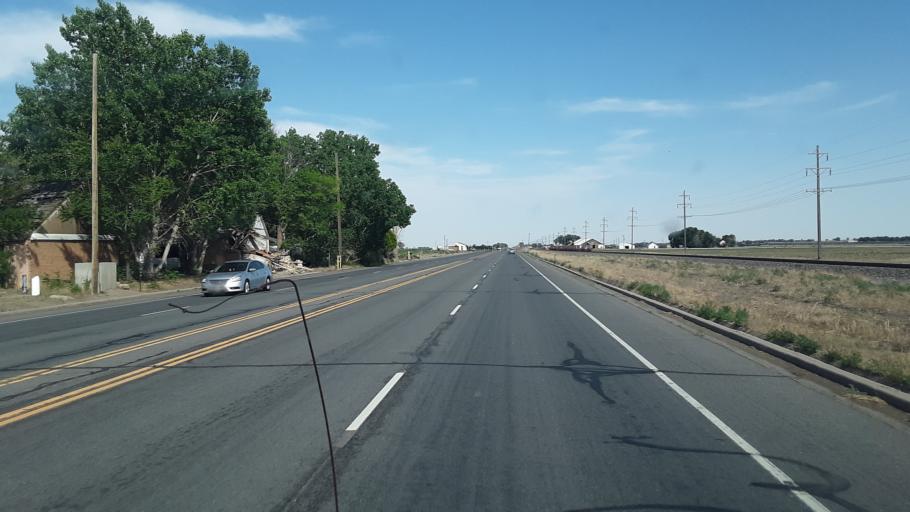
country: US
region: Colorado
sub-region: Otero County
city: Rocky Ford
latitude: 38.0896
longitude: -103.8108
